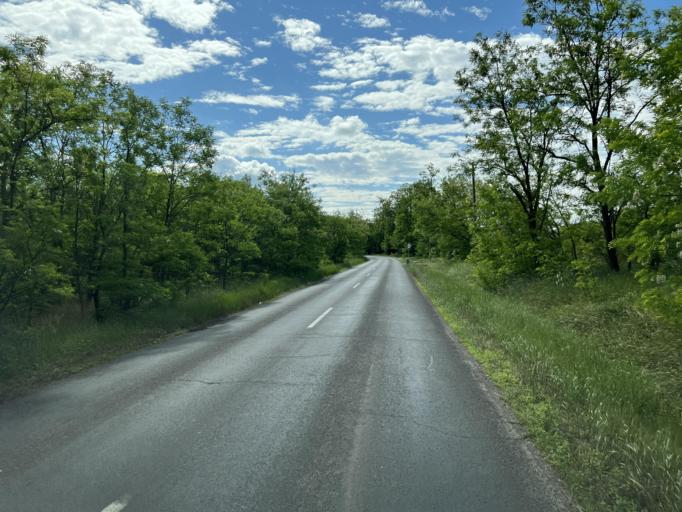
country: HU
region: Pest
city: Godollo
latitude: 47.5802
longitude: 19.3961
